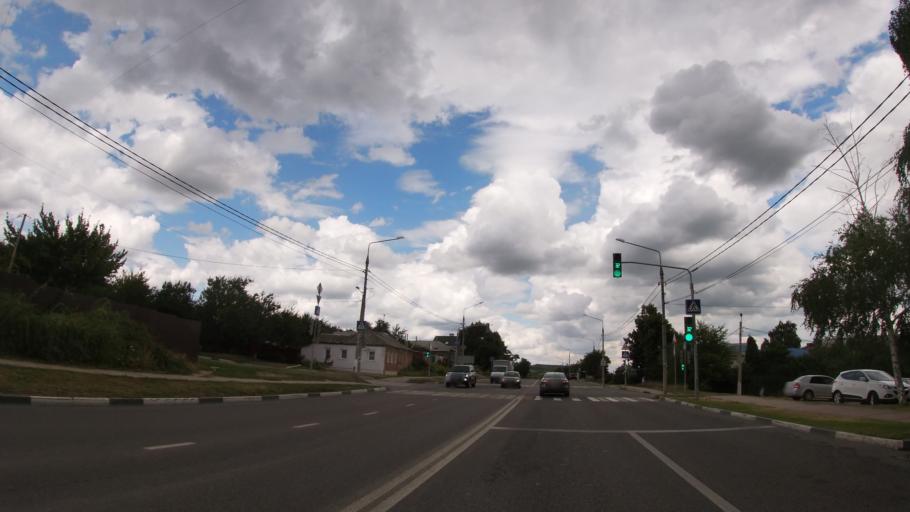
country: RU
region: Belgorod
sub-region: Belgorodskiy Rayon
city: Belgorod
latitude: 50.6025
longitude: 36.6097
